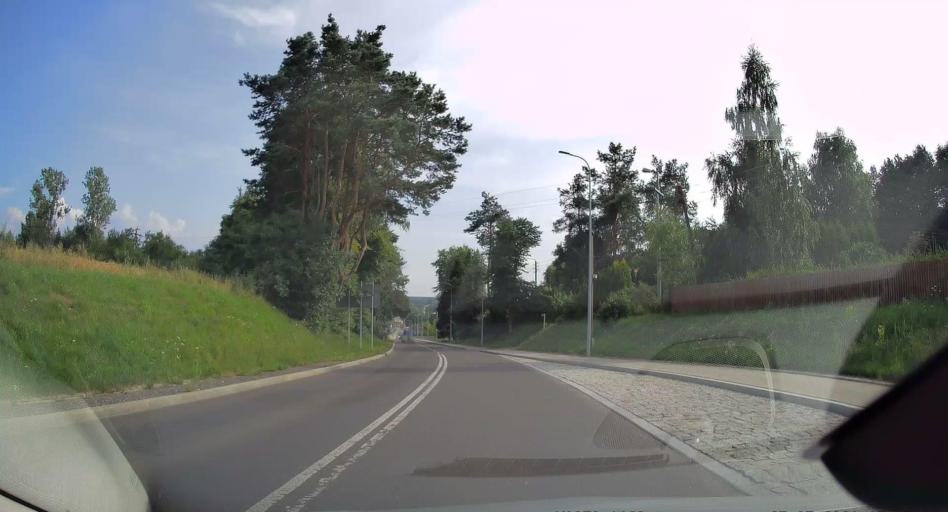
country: PL
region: Lodz Voivodeship
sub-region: Powiat tomaszowski
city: Inowlodz
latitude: 51.5304
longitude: 20.2229
